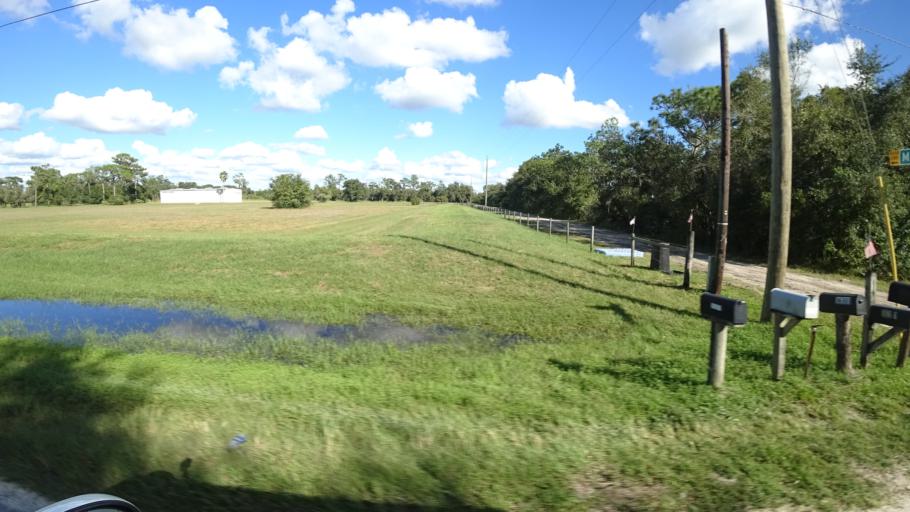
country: US
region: Florida
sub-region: Sarasota County
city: Lake Sarasota
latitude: 27.3824
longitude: -82.2683
